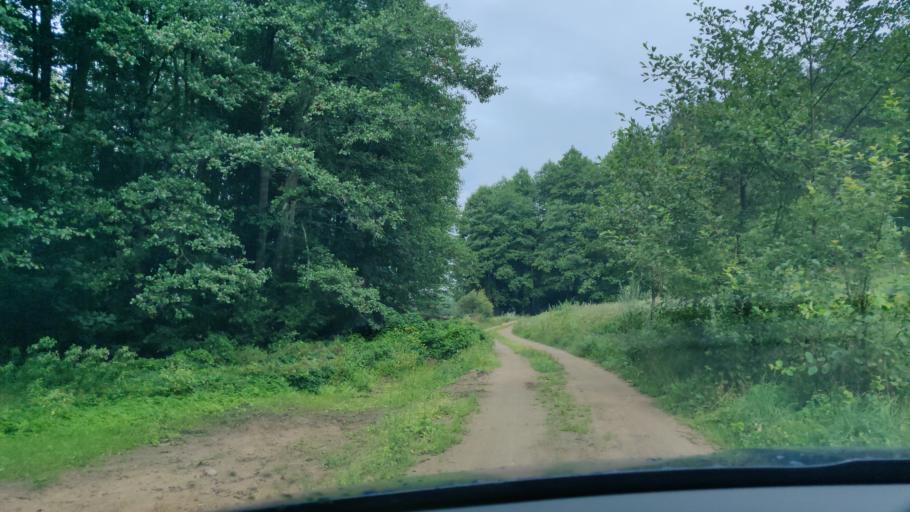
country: LT
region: Vilnius County
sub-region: Trakai
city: Rudiskes
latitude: 54.6078
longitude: 24.8410
